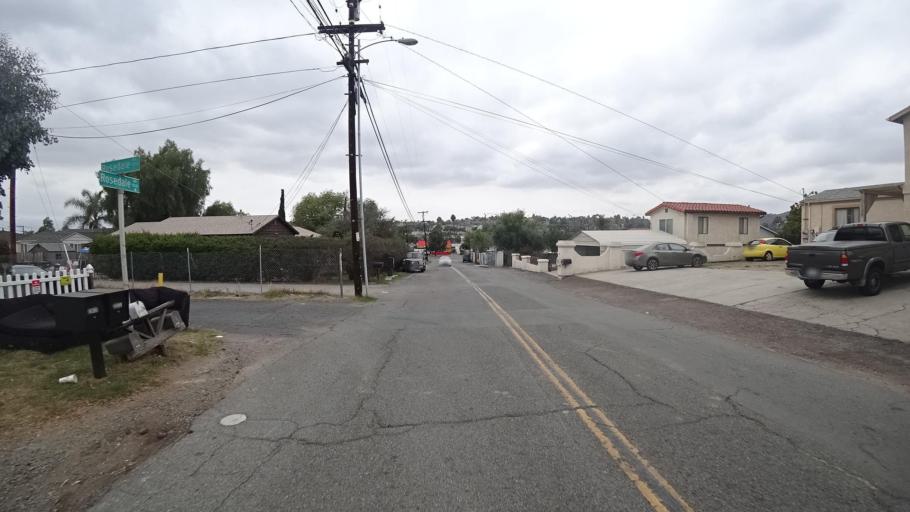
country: US
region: California
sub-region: San Diego County
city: Spring Valley
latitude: 32.7362
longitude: -117.0054
